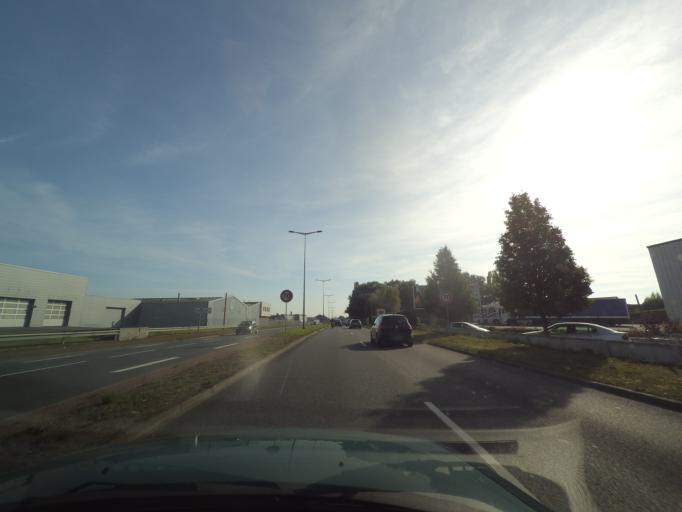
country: FR
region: Pays de la Loire
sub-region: Departement de Maine-et-Loire
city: Cholet
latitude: 47.0735
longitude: -0.8667
